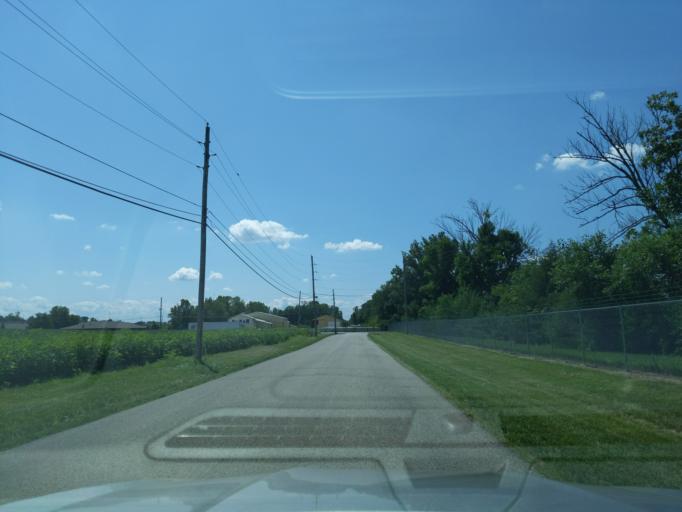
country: US
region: Indiana
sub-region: Decatur County
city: Greensburg
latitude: 39.3580
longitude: -85.4891
